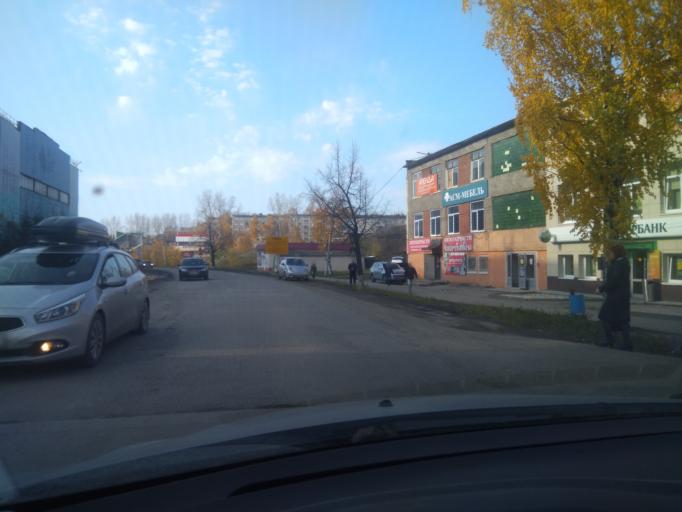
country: RU
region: Sverdlovsk
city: Nizhniye Sergi
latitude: 56.6646
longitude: 59.3075
